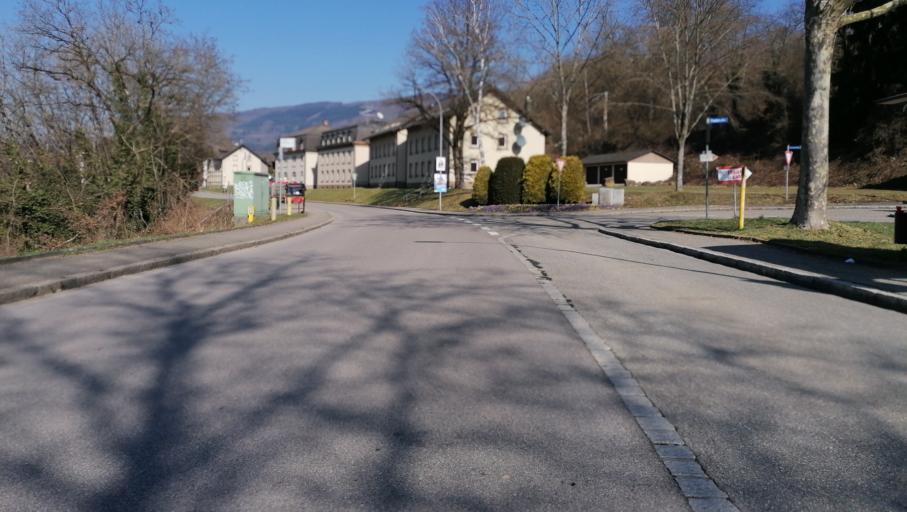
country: DE
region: Baden-Wuerttemberg
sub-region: Freiburg Region
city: Schworstadt
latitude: 47.5861
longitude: 7.9118
